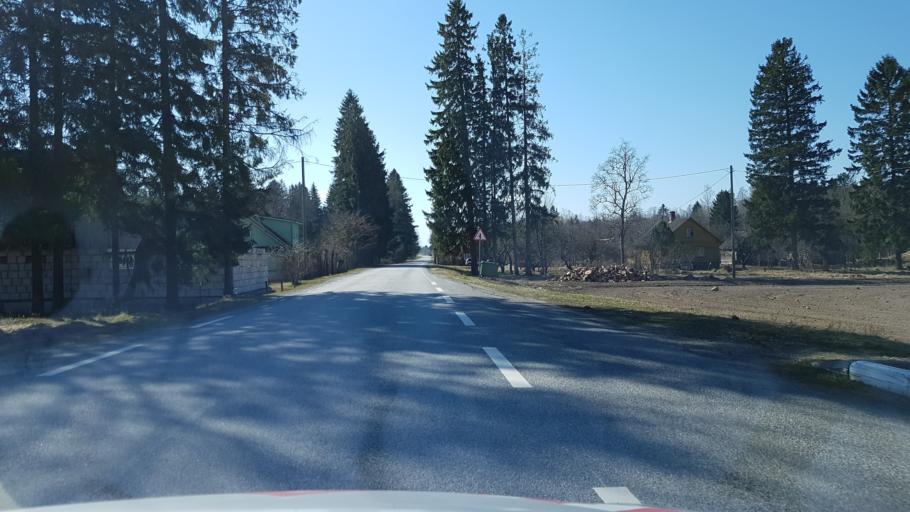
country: EE
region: Ida-Virumaa
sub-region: Kohtla-Nomme vald
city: Kohtla-Nomme
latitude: 59.3024
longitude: 27.2382
